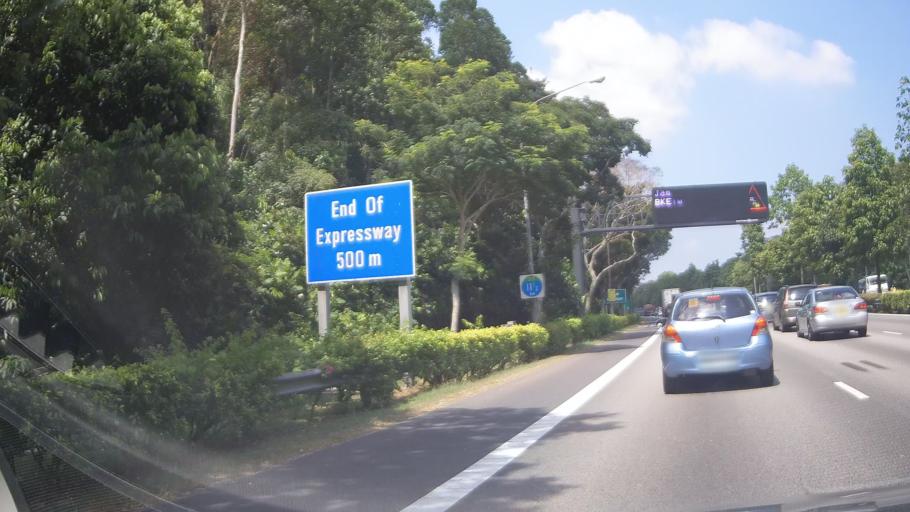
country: MY
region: Johor
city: Johor Bahru
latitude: 1.4256
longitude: 103.7780
